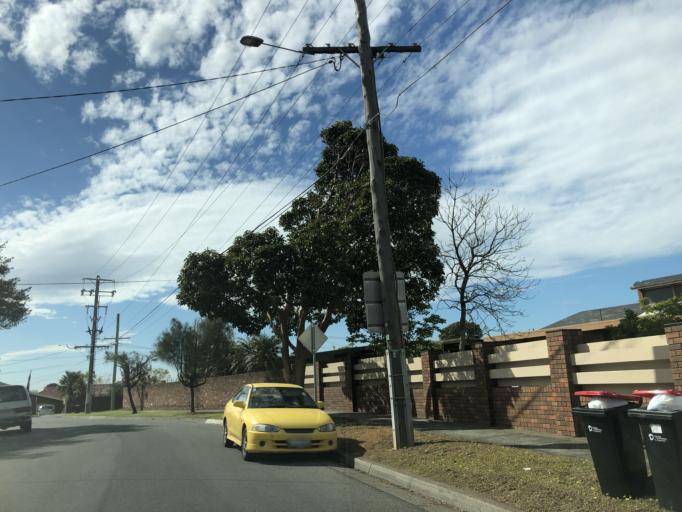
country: AU
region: Victoria
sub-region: Greater Dandenong
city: Dandenong
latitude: -37.9768
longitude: 145.2025
